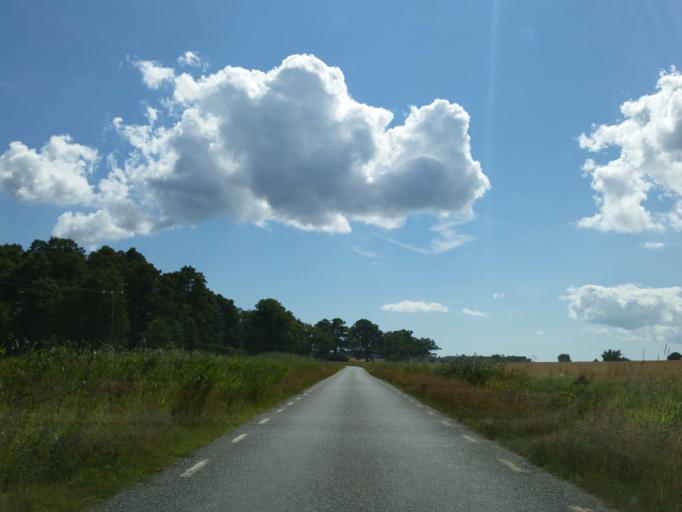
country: SE
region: Stockholm
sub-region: Sodertalje Kommun
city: Pershagen
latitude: 59.0455
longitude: 17.6588
